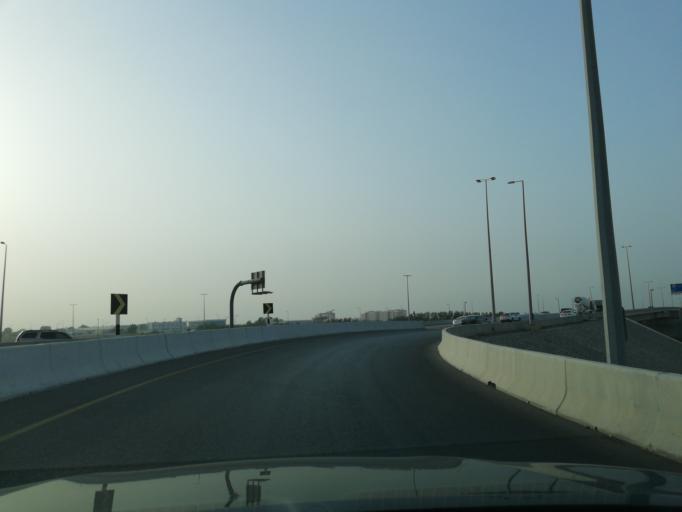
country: OM
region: Muhafazat Masqat
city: Bawshar
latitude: 23.5652
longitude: 58.3790
